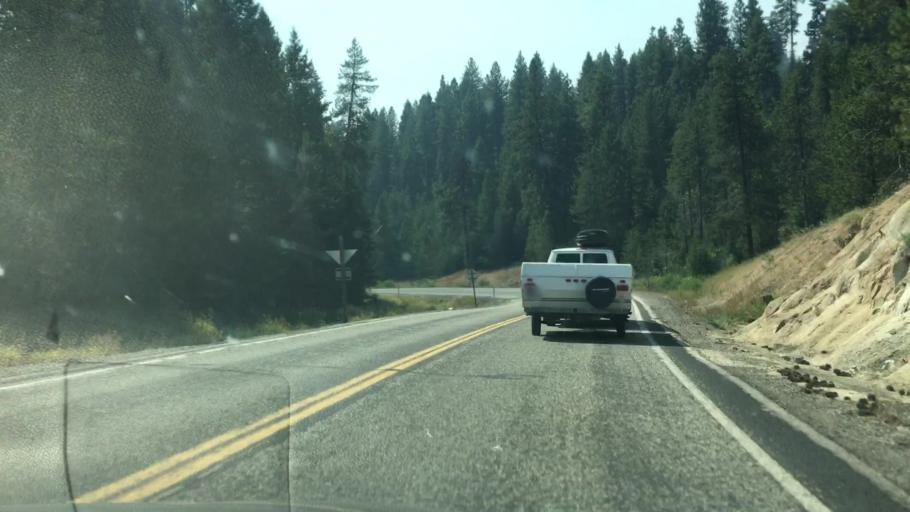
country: US
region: Idaho
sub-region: Valley County
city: Cascade
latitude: 44.3355
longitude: -116.0381
